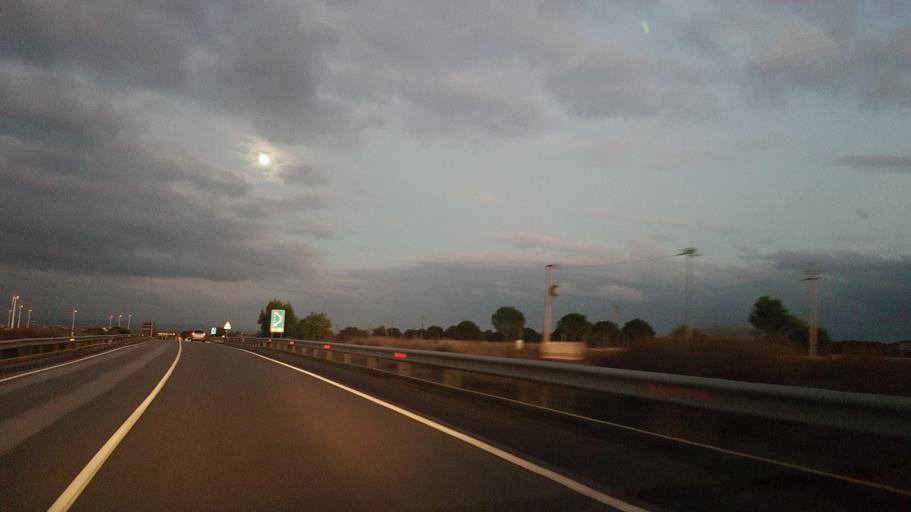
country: IT
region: Apulia
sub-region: Provincia di Taranto
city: Laterza
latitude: 40.6487
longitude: 16.8282
